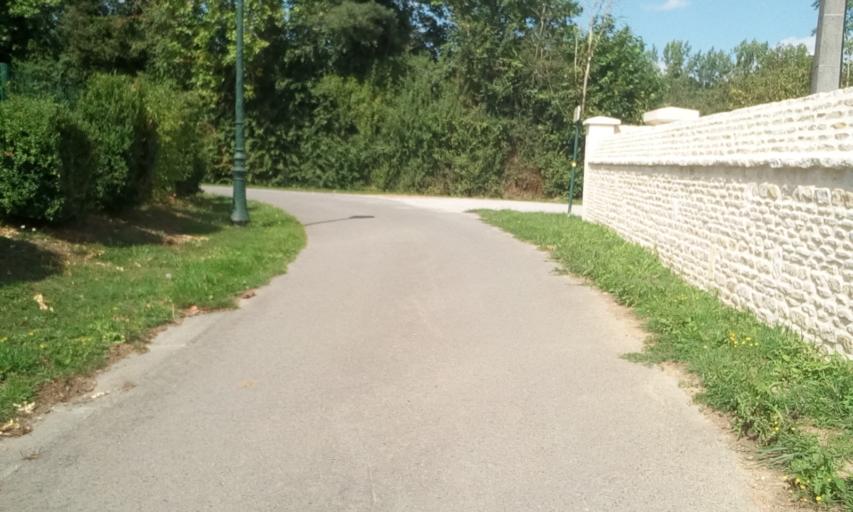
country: FR
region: Lower Normandy
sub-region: Departement du Calvados
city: Argences
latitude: 49.1484
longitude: -0.1124
